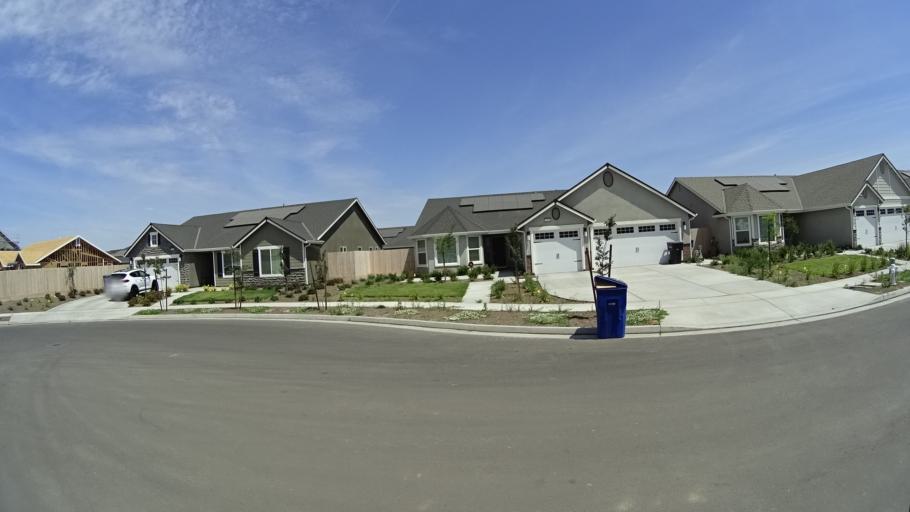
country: US
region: California
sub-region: Kings County
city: Lucerne
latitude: 36.3485
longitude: -119.6837
